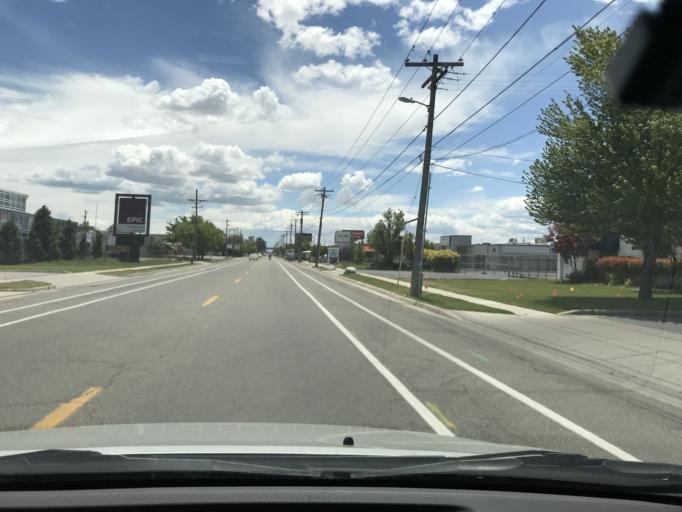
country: US
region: Utah
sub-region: Salt Lake County
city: Centerfield
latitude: 40.6954
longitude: -111.8998
